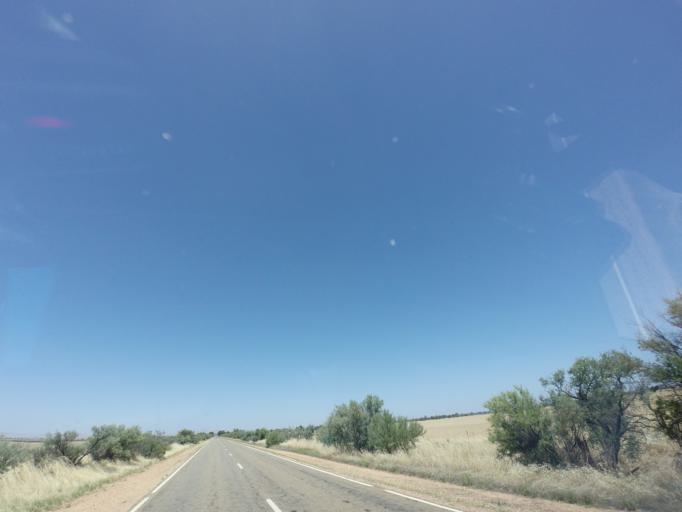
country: AU
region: South Australia
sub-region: Flinders Ranges
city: Quorn
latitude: -32.6663
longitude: 138.1691
